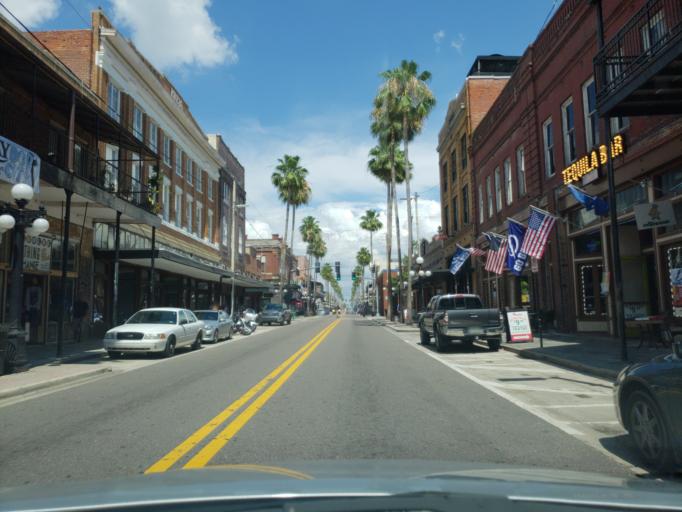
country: US
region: Florida
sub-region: Hillsborough County
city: Tampa
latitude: 27.9602
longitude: -82.4415
